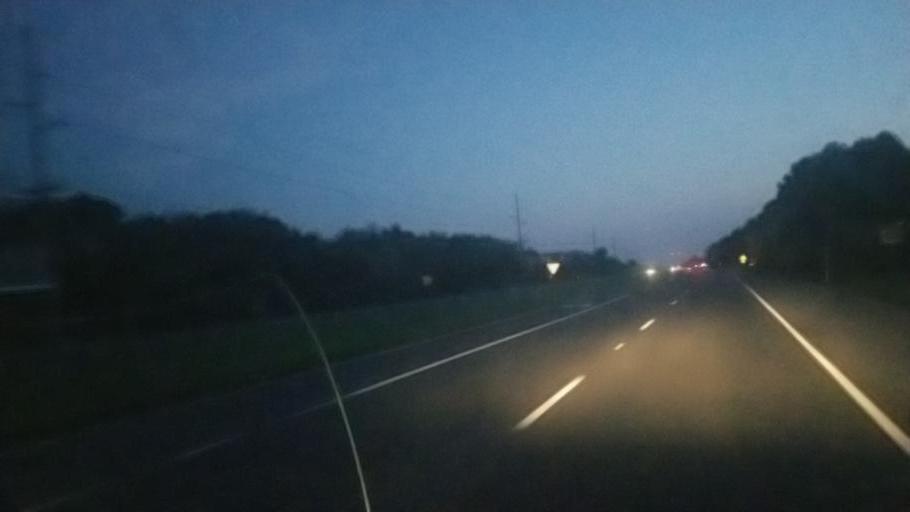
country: US
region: Delaware
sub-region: Sussex County
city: Bethany Beach
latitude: 38.5758
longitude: -75.0605
